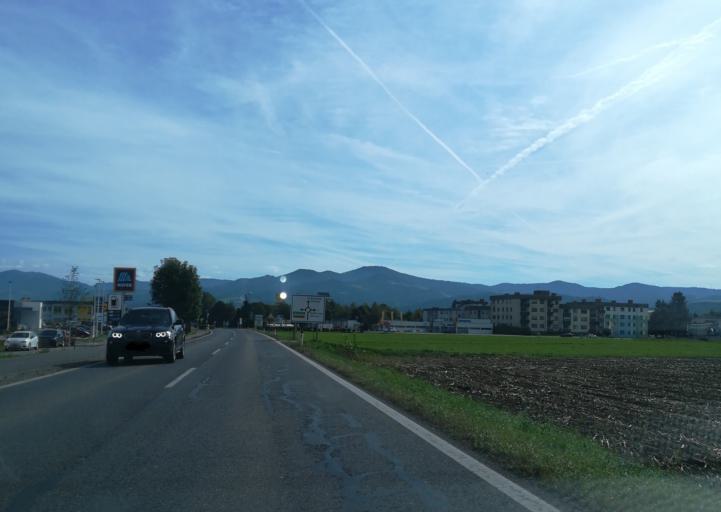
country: AT
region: Styria
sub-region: Politischer Bezirk Murtal
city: Zeltweg
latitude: 47.1947
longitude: 14.7397
